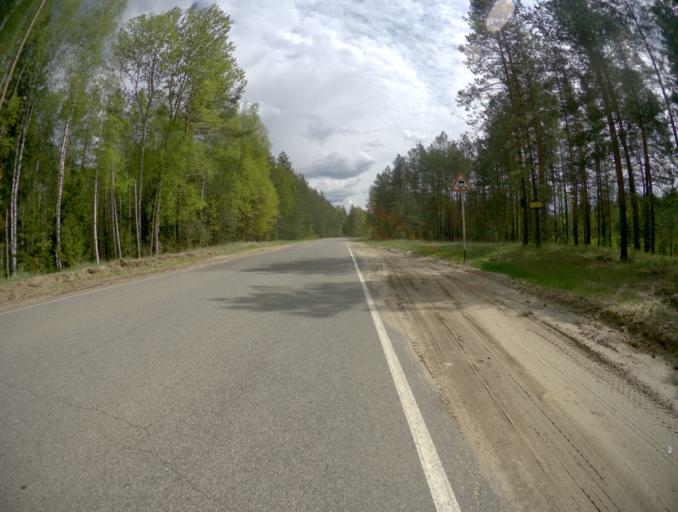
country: RU
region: Vladimir
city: Velikodvorskiy
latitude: 55.3987
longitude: 40.6832
